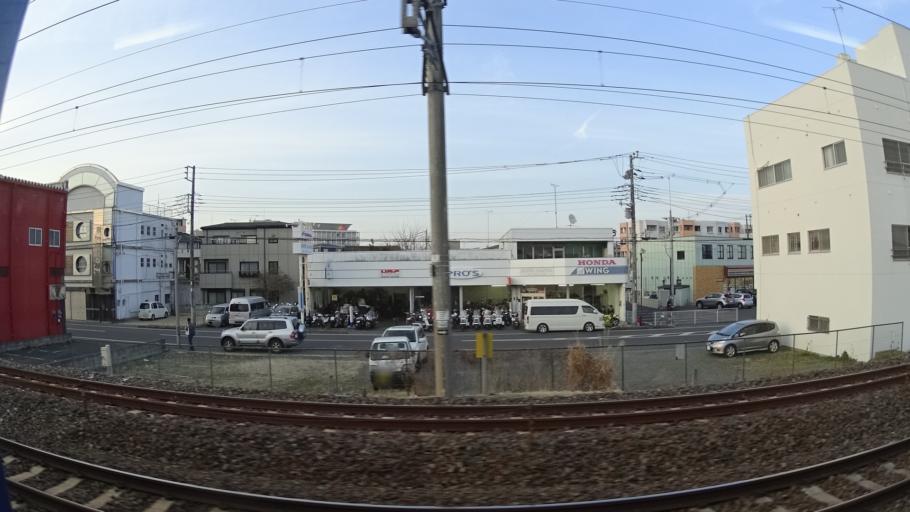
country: JP
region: Ibaraki
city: Katsuta
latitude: 36.3687
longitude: 140.4876
